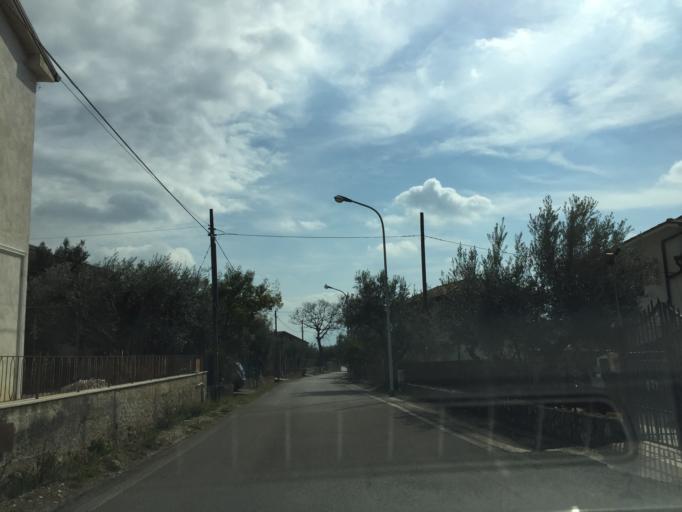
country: IT
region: Latium
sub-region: Provincia di Frosinone
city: Castrocielo
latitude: 41.5289
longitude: 13.6993
